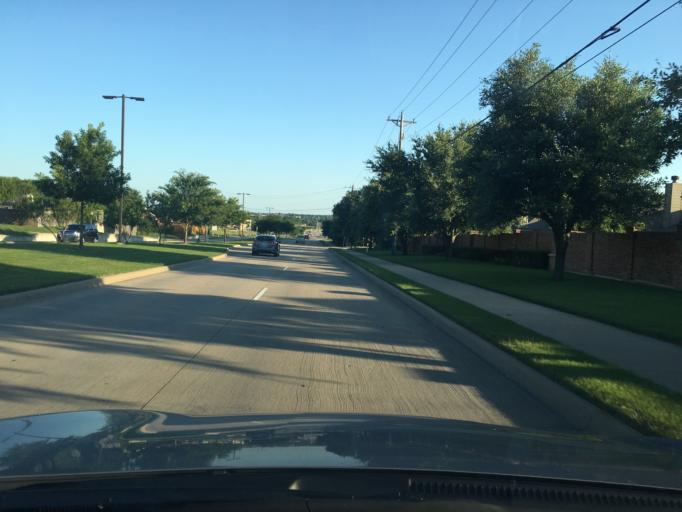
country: US
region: Texas
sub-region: Collin County
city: McKinney
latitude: 33.2236
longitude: -96.6792
